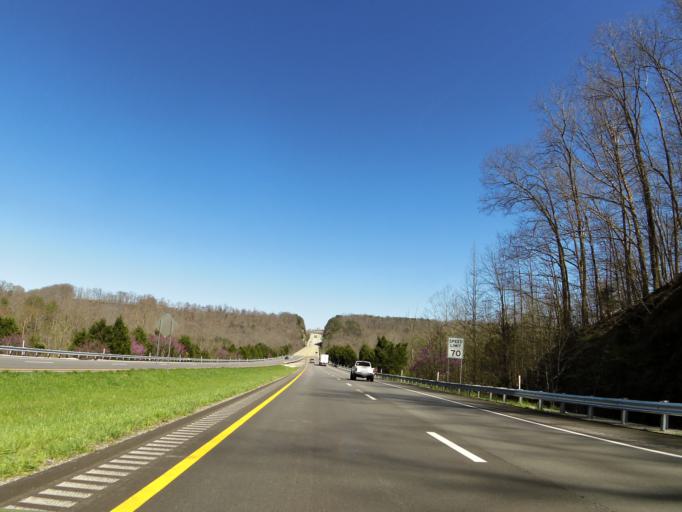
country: US
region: Kentucky
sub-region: Pulaski County
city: Somerset
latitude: 37.0967
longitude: -84.6984
